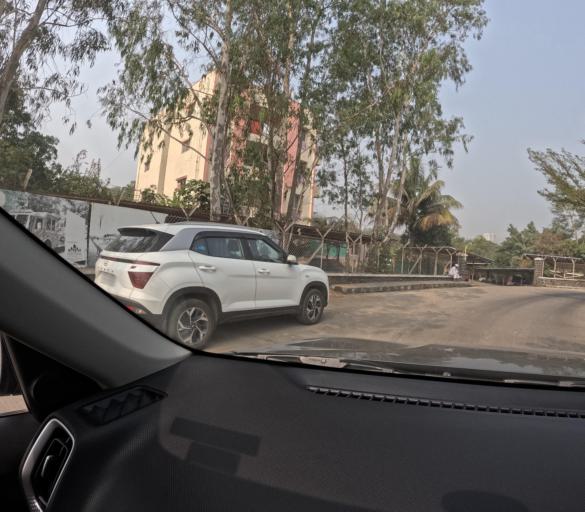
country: IN
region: Maharashtra
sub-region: Pune Division
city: Kharakvasla
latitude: 18.5013
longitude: 73.7379
